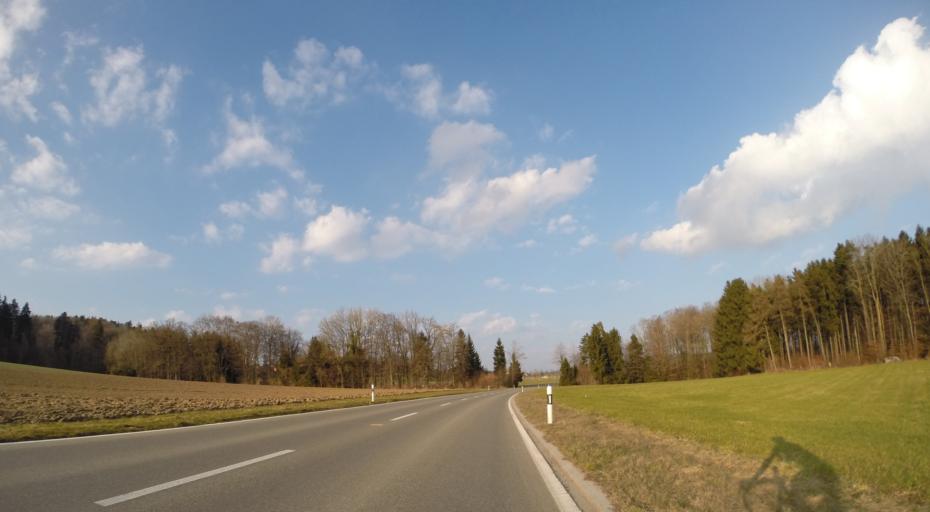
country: CH
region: Thurgau
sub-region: Frauenfeld District
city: Pfyn
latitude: 47.6265
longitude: 8.9601
